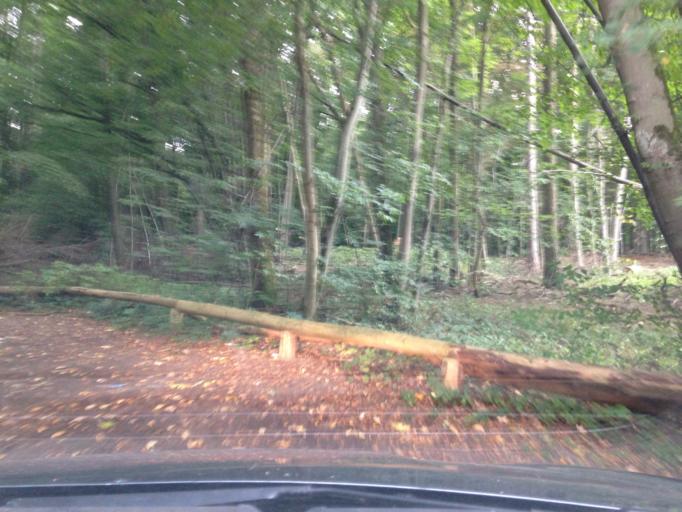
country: DE
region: Mecklenburg-Vorpommern
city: Carpin
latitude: 53.3539
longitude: 13.2298
